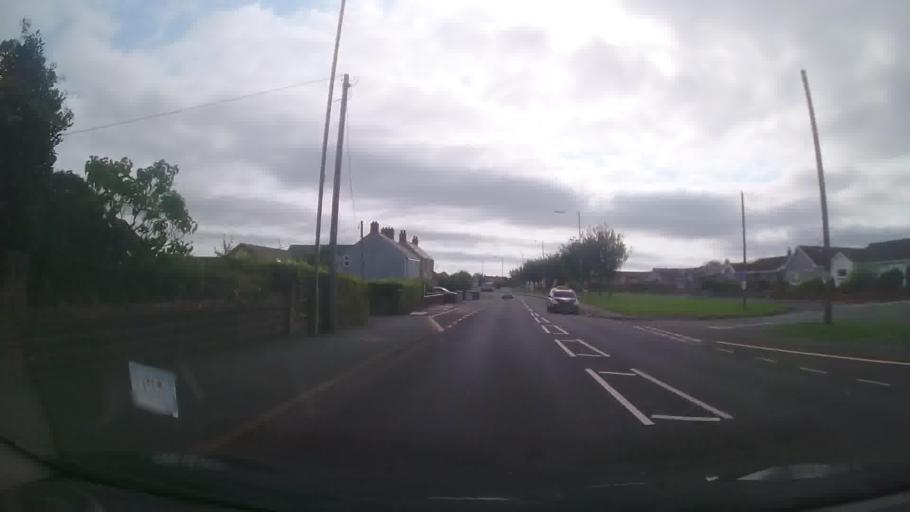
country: GB
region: Wales
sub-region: Pembrokeshire
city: Steynton
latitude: 51.7284
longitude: -5.0177
